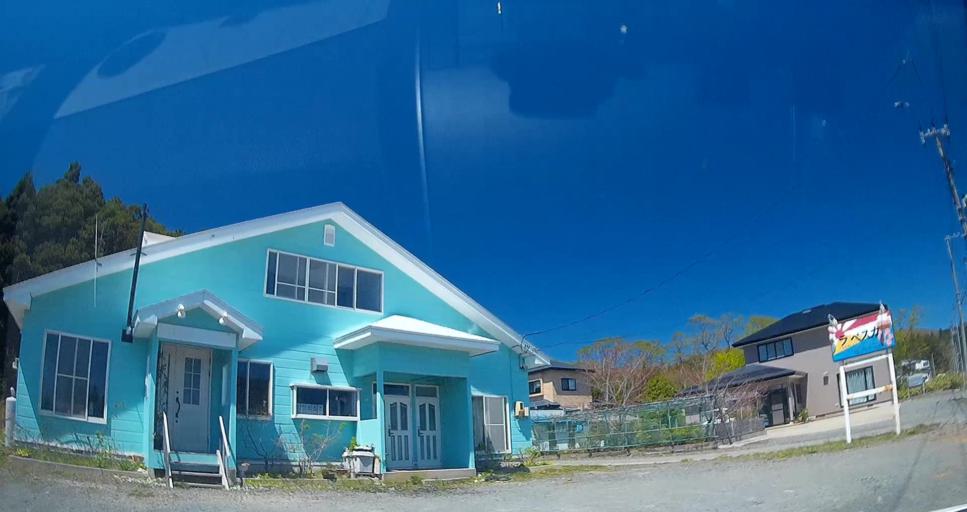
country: JP
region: Aomori
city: Mutsu
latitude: 41.0831
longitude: 141.3856
